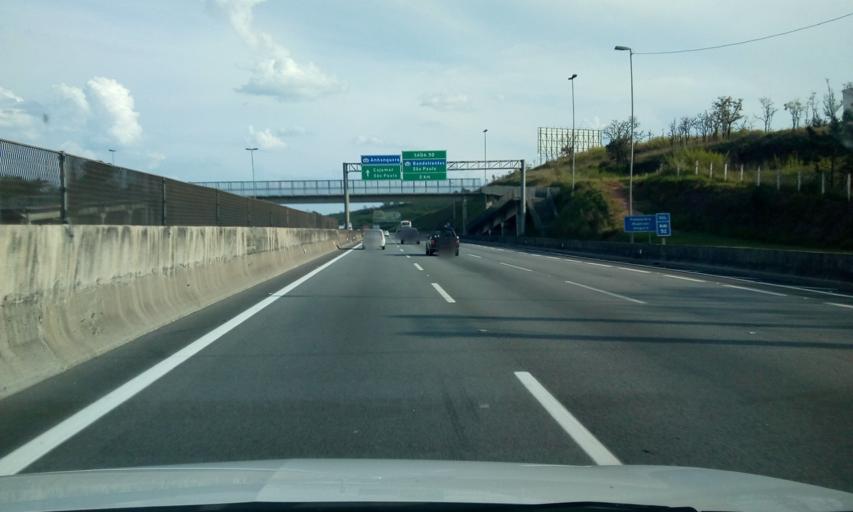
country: BR
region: Sao Paulo
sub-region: Varzea Paulista
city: Varzea Paulista
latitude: -23.2396
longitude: -46.8692
